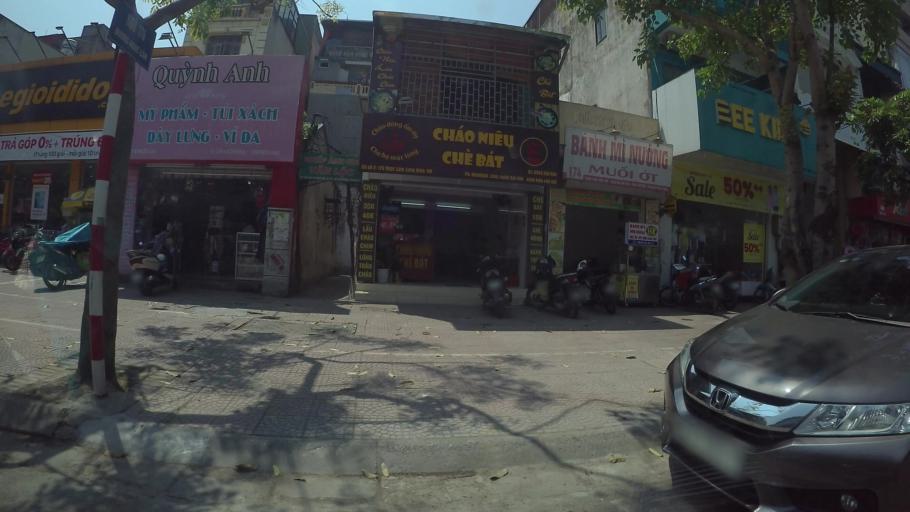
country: VN
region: Ha Noi
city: Hoan Kiem
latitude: 21.0463
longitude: 105.8706
